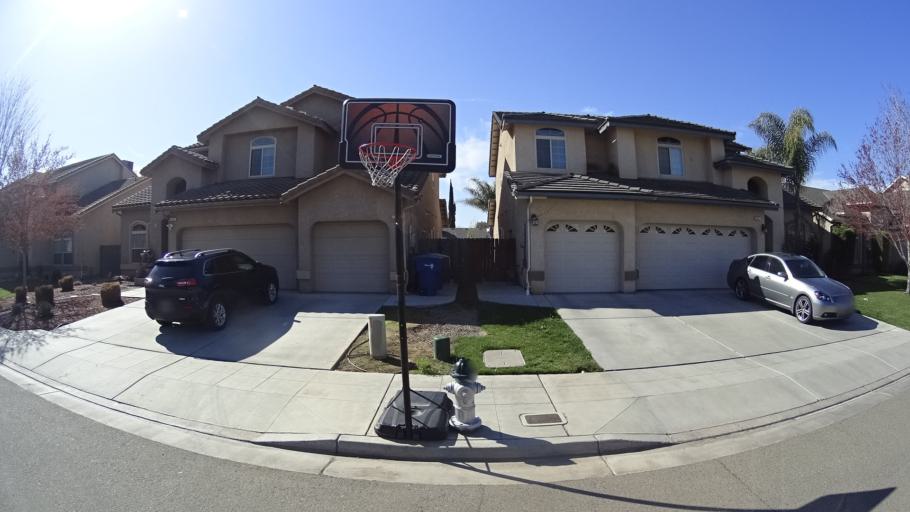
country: US
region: California
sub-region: Fresno County
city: West Park
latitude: 36.7995
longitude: -119.8868
